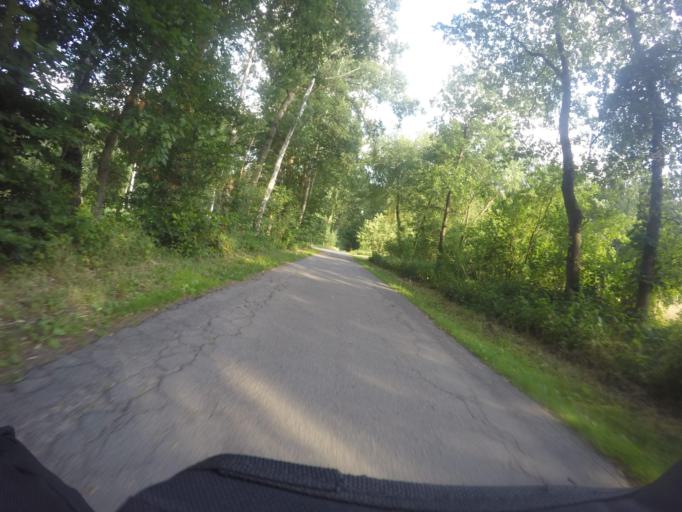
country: DE
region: Lower Saxony
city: Dahlenburg
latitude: 53.2044
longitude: 10.7182
